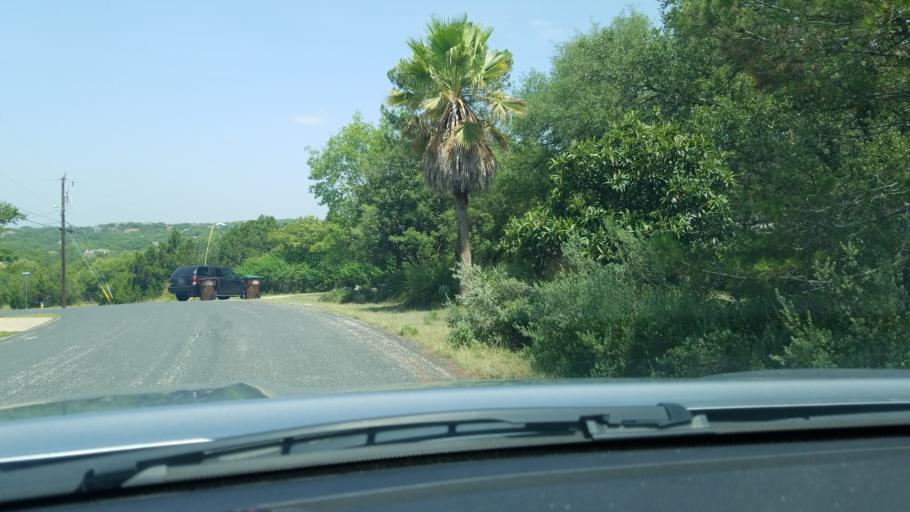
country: US
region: Texas
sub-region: Bexar County
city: Timberwood Park
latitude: 29.6938
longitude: -98.4864
